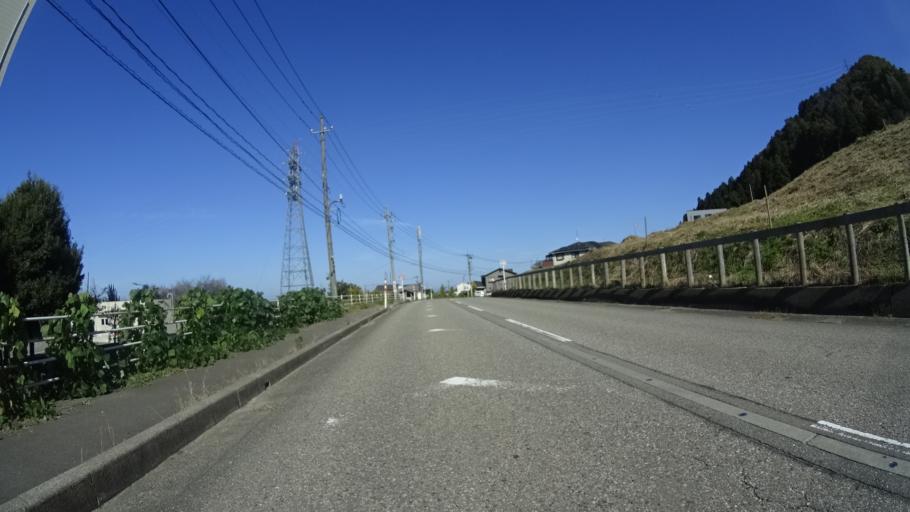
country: JP
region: Ishikawa
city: Nonoichi
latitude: 36.4949
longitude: 136.6204
